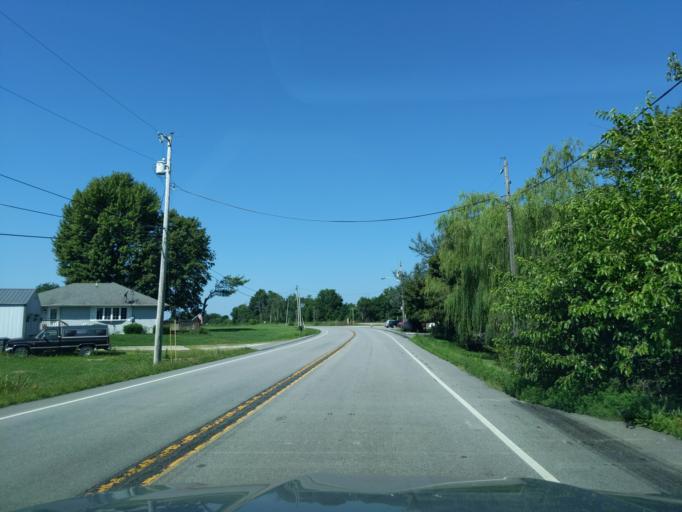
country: US
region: Indiana
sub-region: Ripley County
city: Osgood
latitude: 39.0731
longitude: -85.3896
